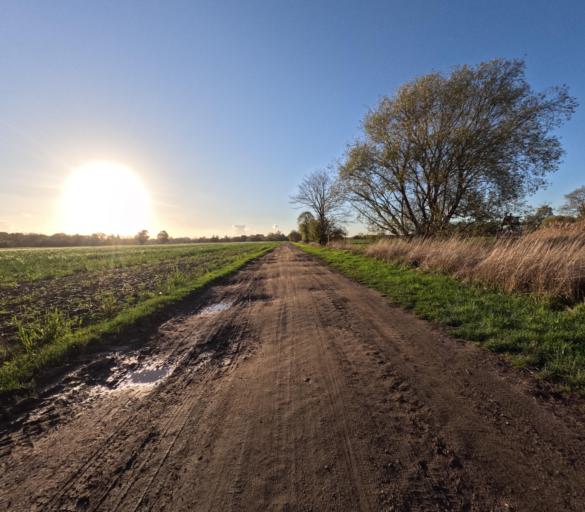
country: DE
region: Saxony-Anhalt
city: Zoschen
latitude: 51.3643
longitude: 12.1257
